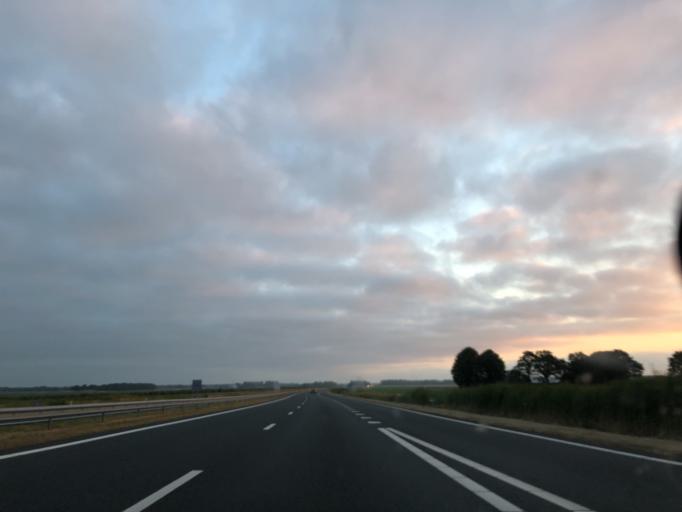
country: NL
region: Groningen
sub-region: Gemeente Veendam
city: Veendam
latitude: 53.1373
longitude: 6.8990
